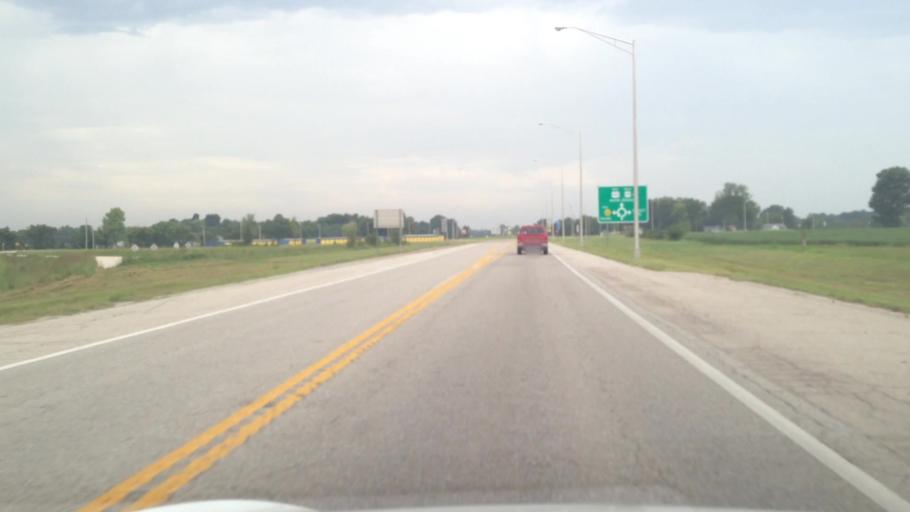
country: US
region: Kansas
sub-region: Cherokee County
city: Baxter Springs
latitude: 37.0778
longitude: -94.7137
